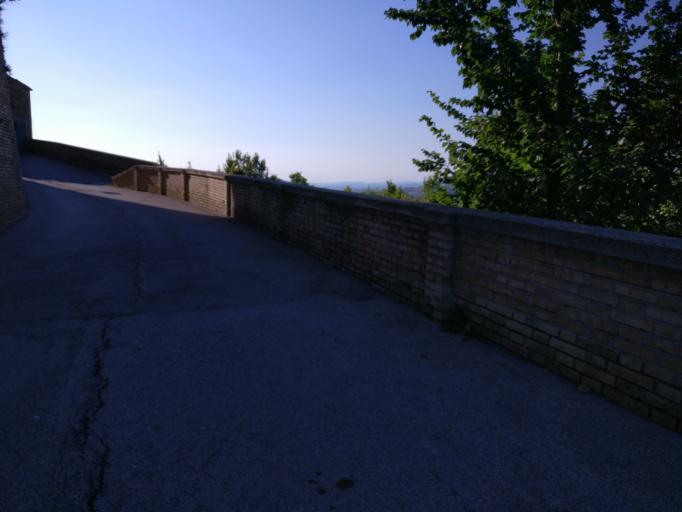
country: IT
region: The Marches
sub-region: Provincia di Ascoli Piceno
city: Montedinove
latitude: 42.9704
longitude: 13.5860
